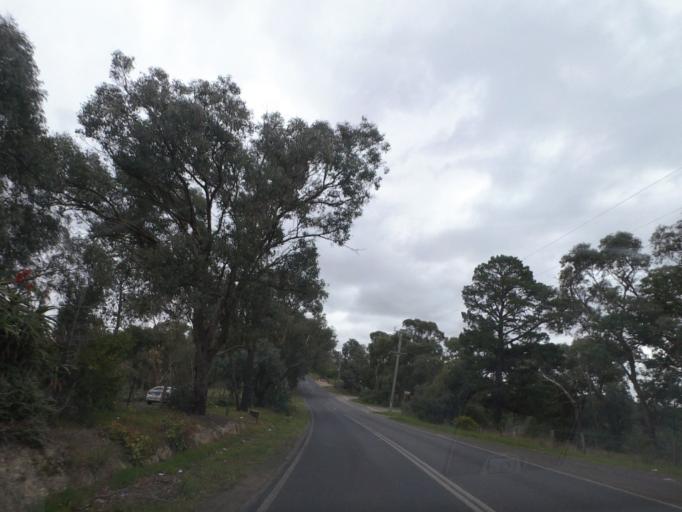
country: AU
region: Victoria
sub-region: Nillumbik
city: Diamond Creek
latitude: -37.6453
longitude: 145.1465
